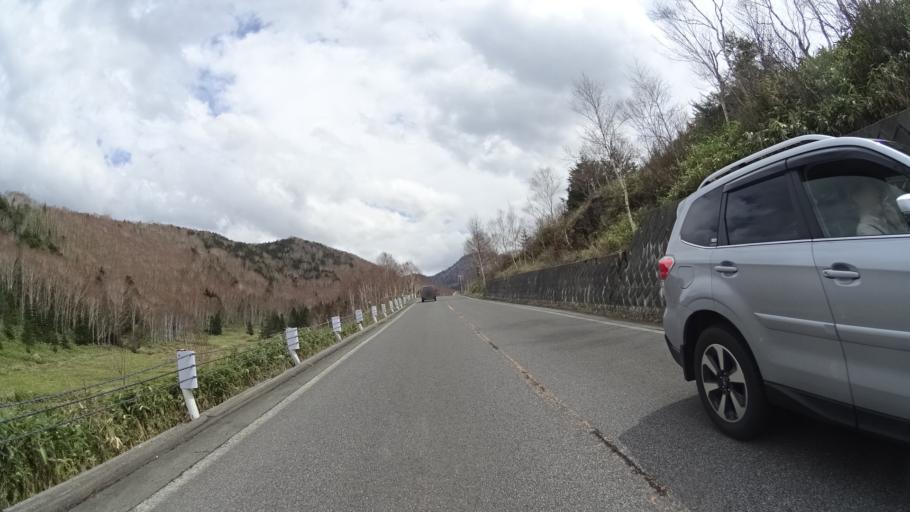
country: JP
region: Nagano
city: Nakano
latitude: 36.6948
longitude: 138.4910
